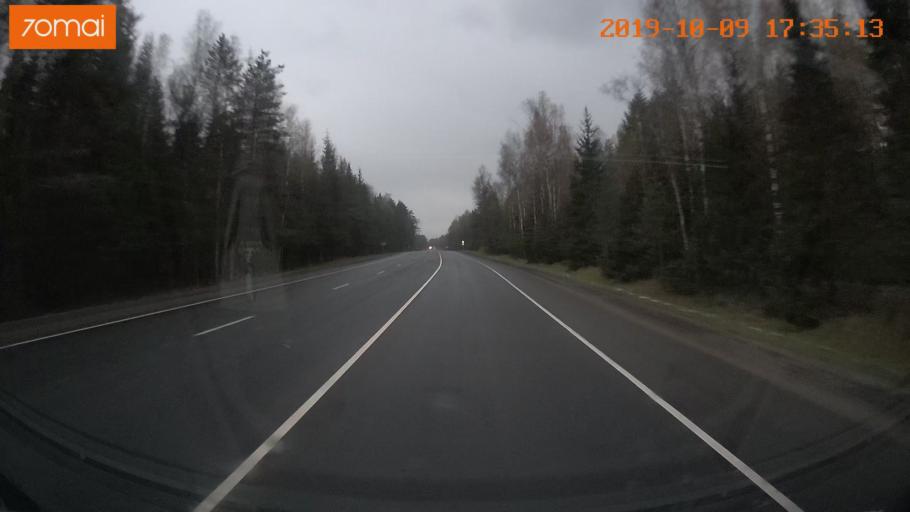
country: RU
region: Ivanovo
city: Bogorodskoye
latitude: 57.0968
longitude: 41.0037
